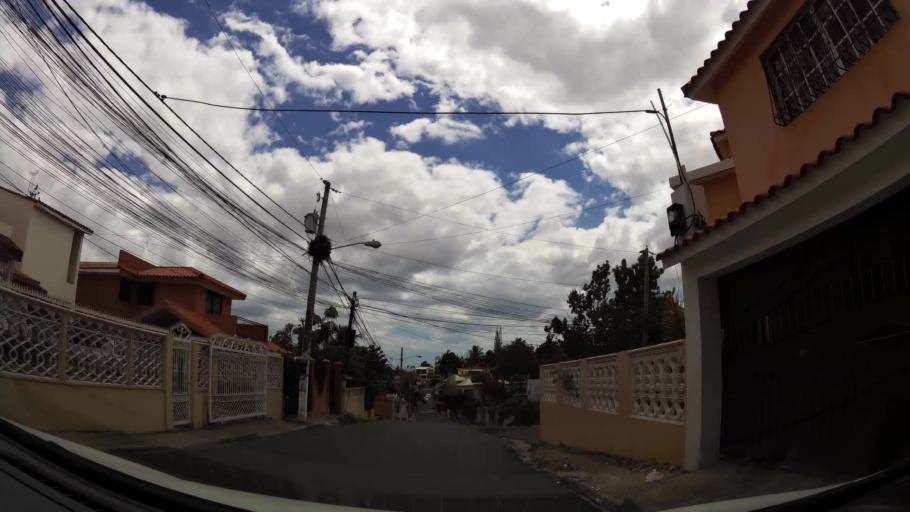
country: DO
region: Nacional
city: Ensanche Luperon
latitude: 18.5255
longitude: -69.9090
